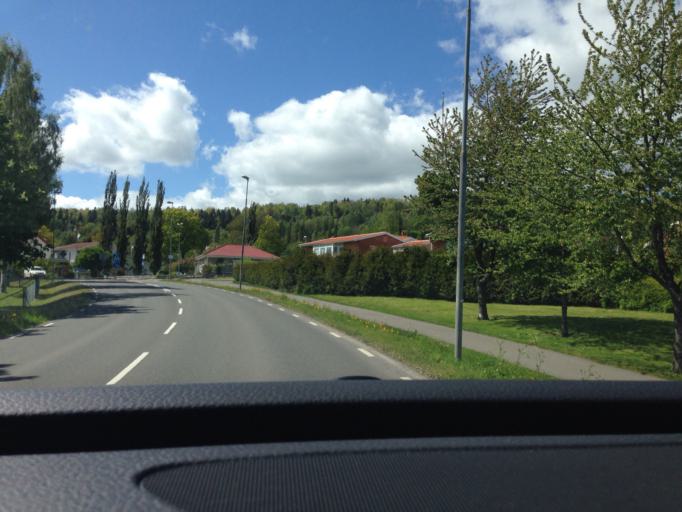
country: SE
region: Vaestra Goetaland
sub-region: Skovde Kommun
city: Skoevde
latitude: 58.4100
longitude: 13.8354
